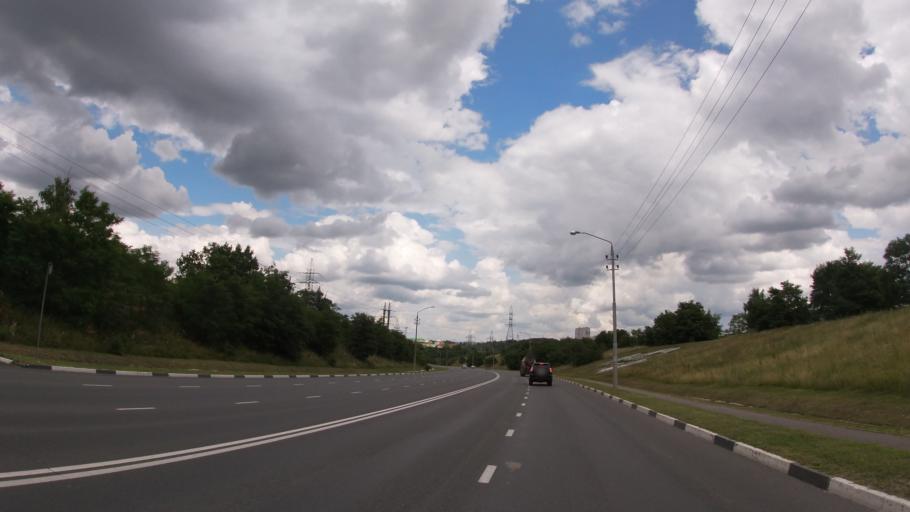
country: RU
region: Belgorod
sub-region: Belgorodskiy Rayon
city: Belgorod
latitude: 50.5556
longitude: 36.5840
